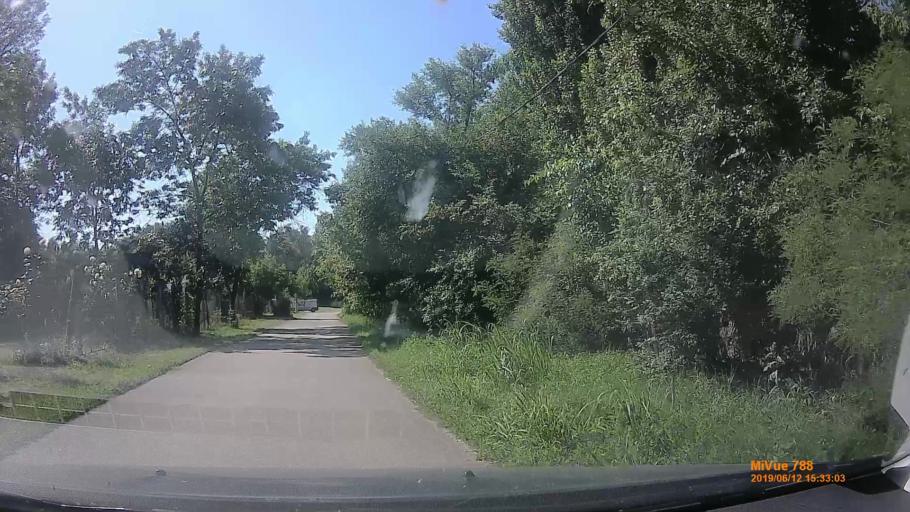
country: HU
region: Csongrad
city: Mako
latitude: 46.1986
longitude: 20.4691
